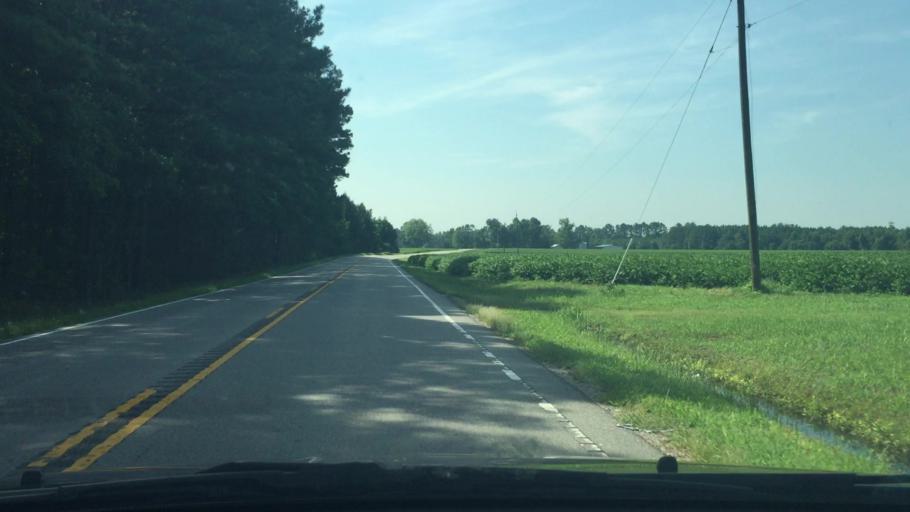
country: US
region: Virginia
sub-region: Southampton County
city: Courtland
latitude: 36.8481
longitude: -77.1330
